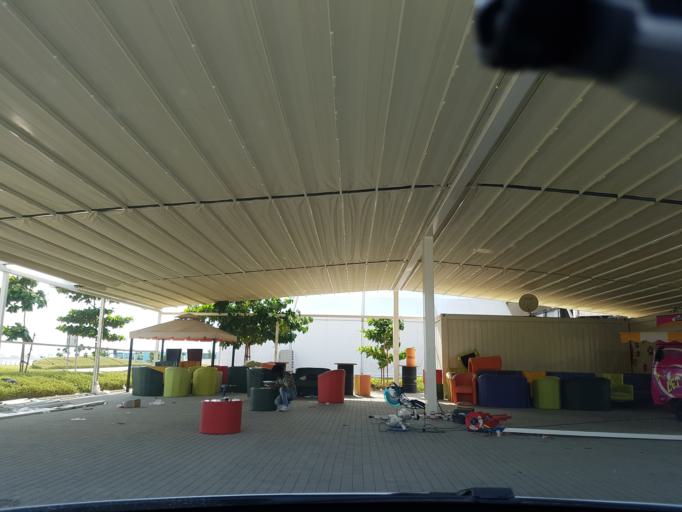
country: AE
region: Ajman
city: Ajman
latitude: 25.4290
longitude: 55.4656
